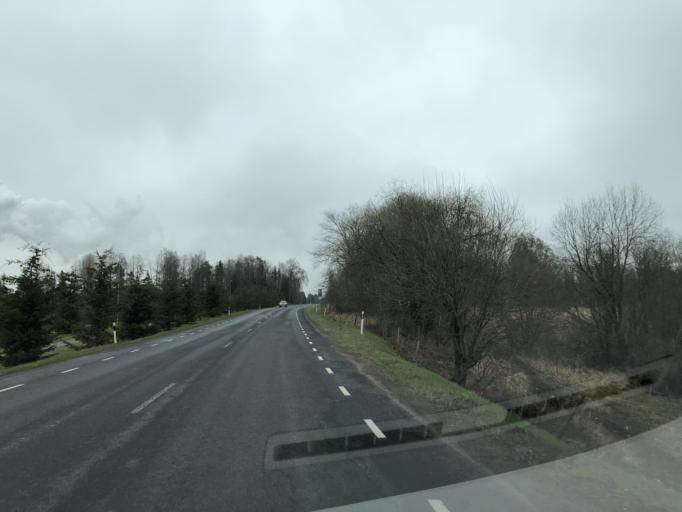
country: EE
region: Laeaene-Virumaa
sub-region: Vaeike-Maarja vald
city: Vaike-Maarja
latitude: 59.1065
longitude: 26.2327
